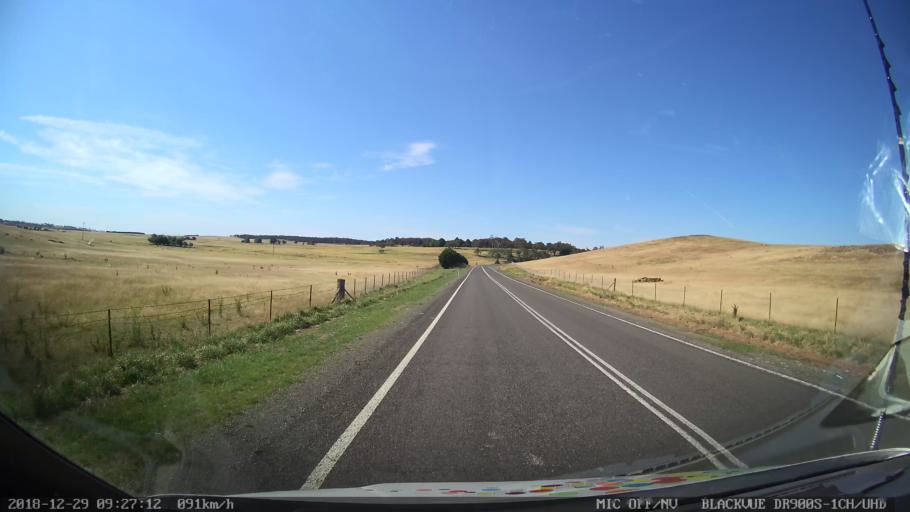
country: AU
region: New South Wales
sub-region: Upper Lachlan Shire
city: Crookwell
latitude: -34.5635
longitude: 149.3857
